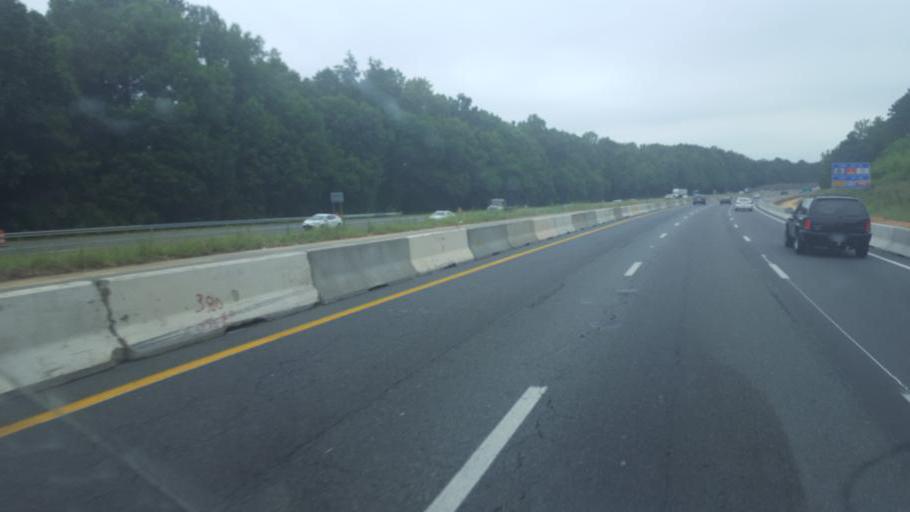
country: US
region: North Carolina
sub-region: Mecklenburg County
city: Charlotte
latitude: 35.2911
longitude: -80.8510
